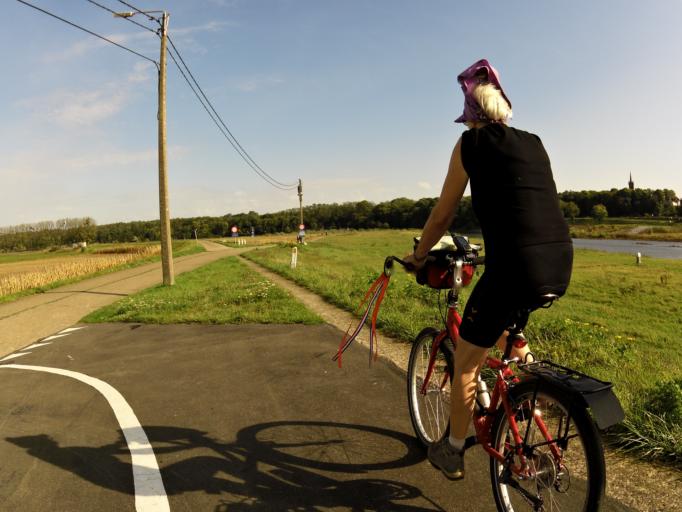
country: NL
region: Limburg
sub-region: Gemeente Stein
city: Elsloo
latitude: 50.9492
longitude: 5.7501
